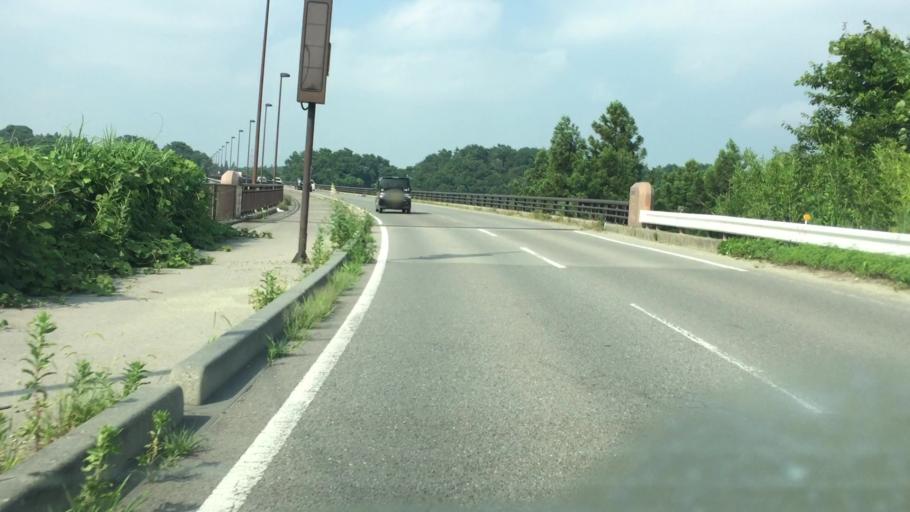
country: JP
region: Tochigi
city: Kuroiso
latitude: 37.0199
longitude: 140.0127
